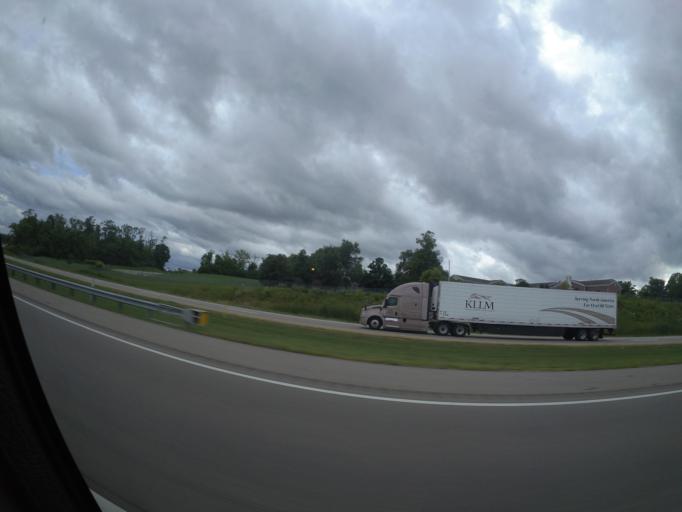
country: US
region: Ohio
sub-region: Montgomery County
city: Vandalia
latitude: 39.8657
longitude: -84.1966
